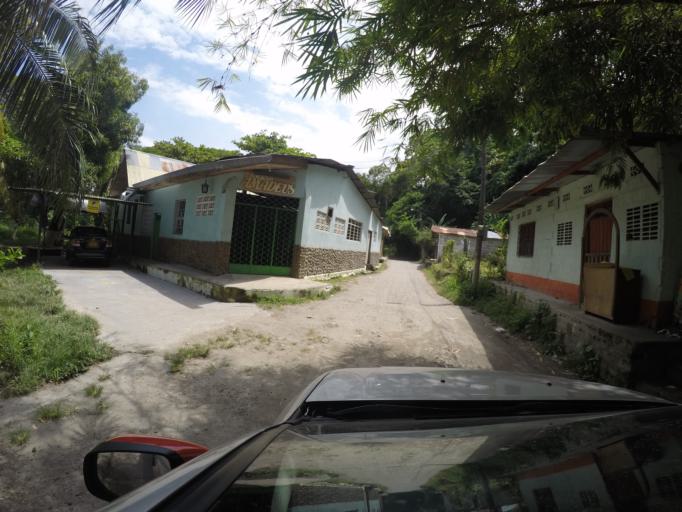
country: CO
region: Caldas
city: La Dorada
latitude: 5.3411
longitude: -74.7357
